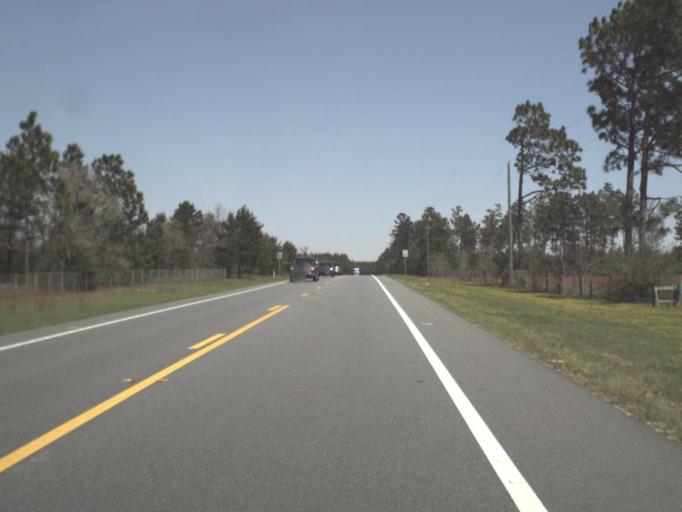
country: US
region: Florida
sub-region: Bay County
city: Youngstown
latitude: 30.4280
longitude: -85.2916
